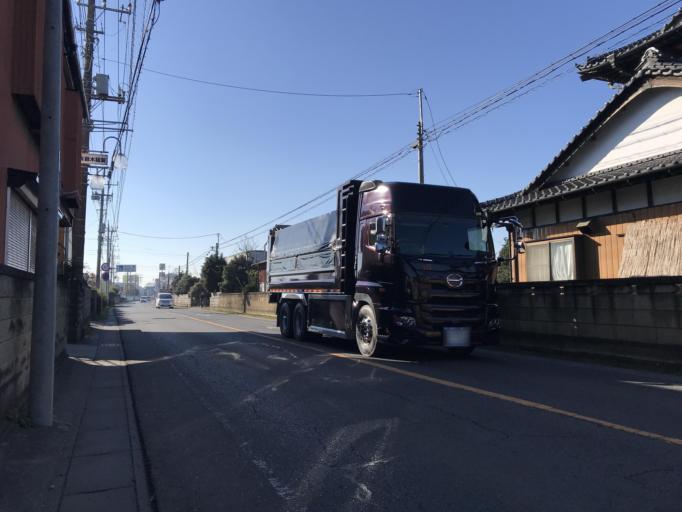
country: JP
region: Ibaraki
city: Sakai
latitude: 36.1917
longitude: 139.8115
